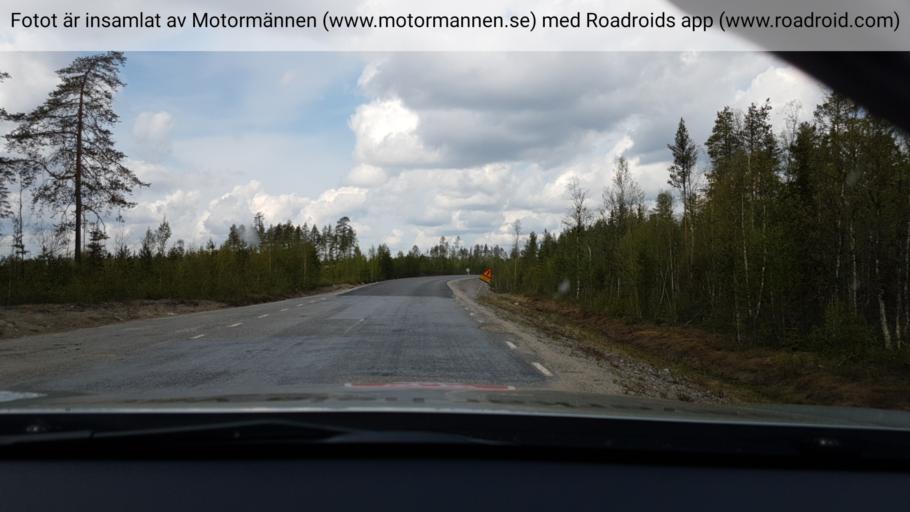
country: SE
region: Vaesterbotten
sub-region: Lycksele Kommun
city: Lycksele
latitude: 63.9787
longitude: 18.4901
